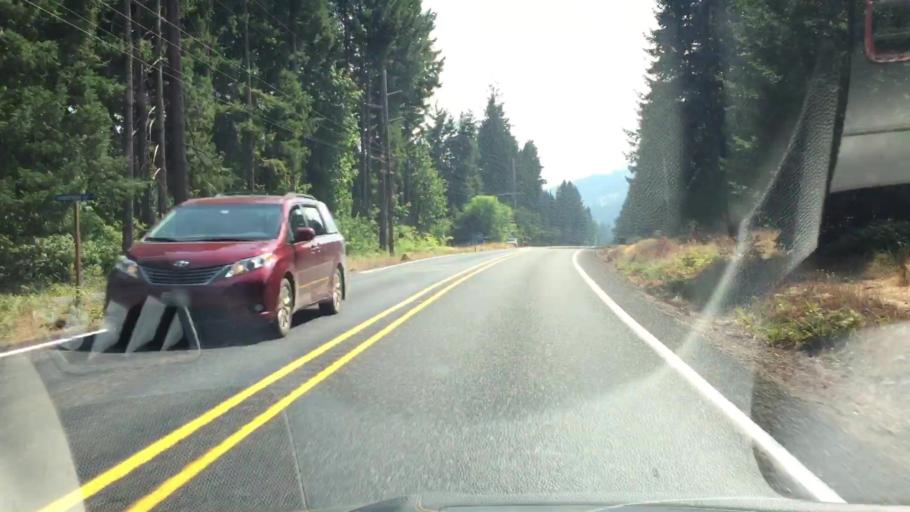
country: US
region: Washington
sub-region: Klickitat County
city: White Salmon
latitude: 45.8644
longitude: -121.5106
